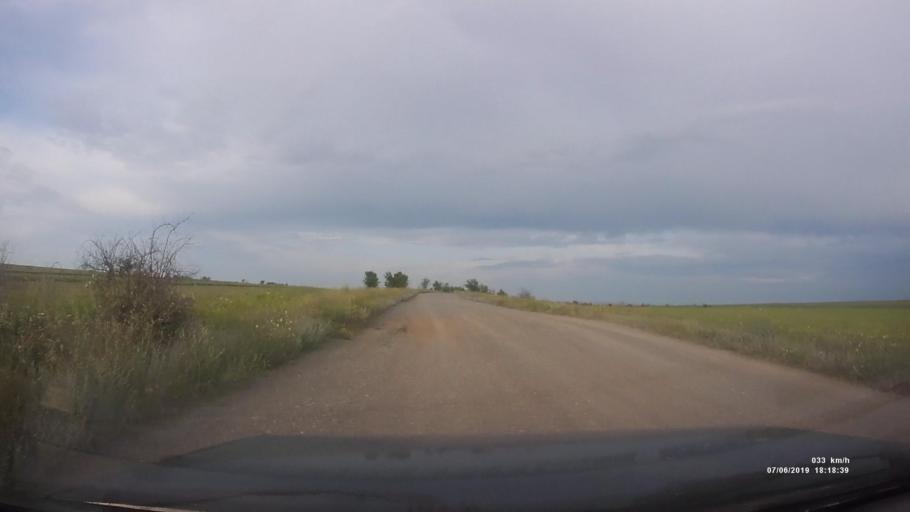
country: RU
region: Rostov
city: Staraya Stanitsa
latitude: 48.2557
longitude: 40.3645
